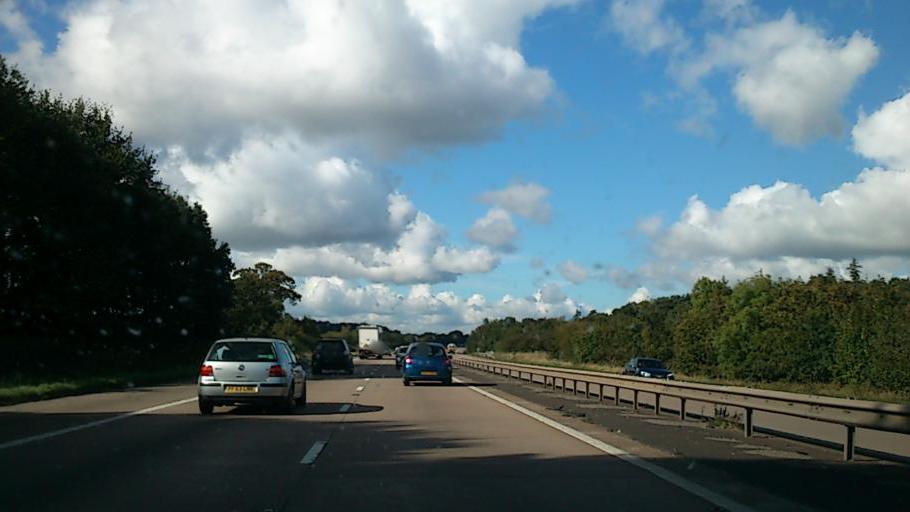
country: GB
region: England
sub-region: Staffordshire
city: Brewood
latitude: 52.6392
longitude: -2.1511
